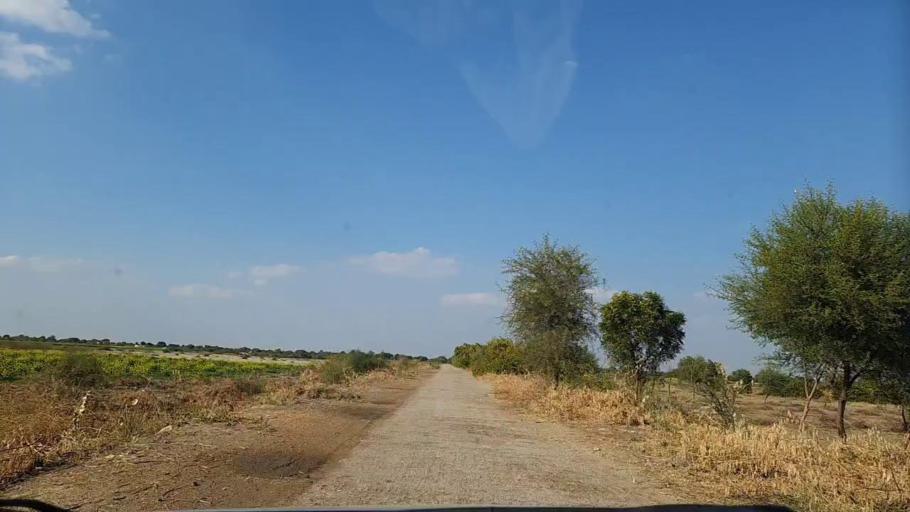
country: PK
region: Sindh
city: Pithoro
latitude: 25.6219
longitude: 69.3544
